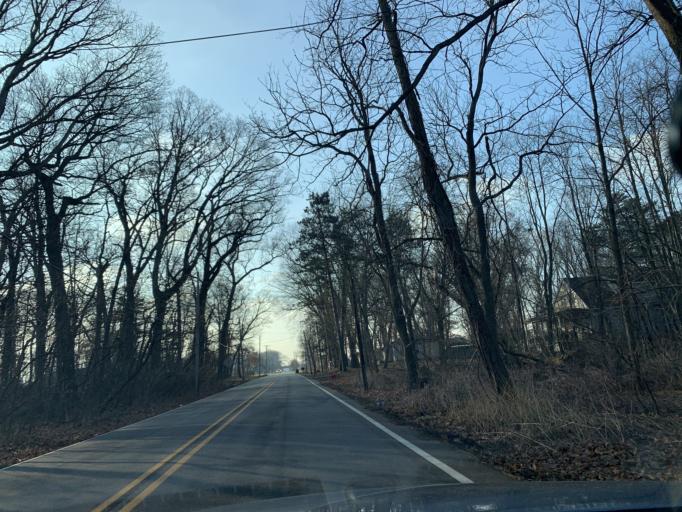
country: US
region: Indiana
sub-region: Porter County
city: Portage
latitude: 41.5805
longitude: -87.1535
